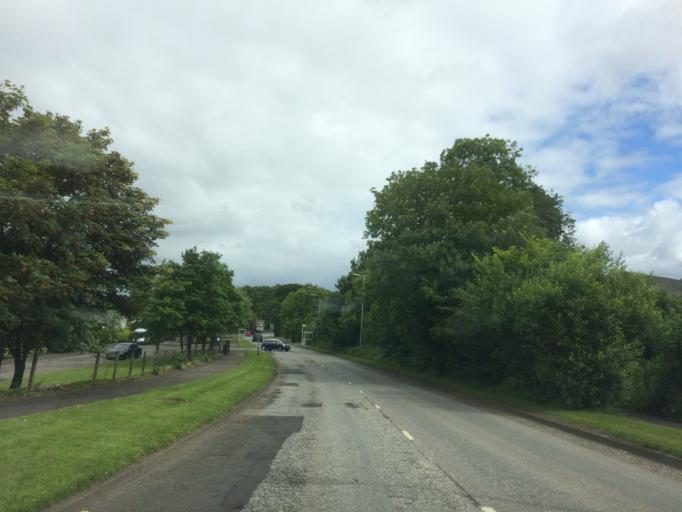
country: GB
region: Scotland
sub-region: East Renfrewshire
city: Newton Mearns
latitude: 55.7763
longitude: -4.3322
